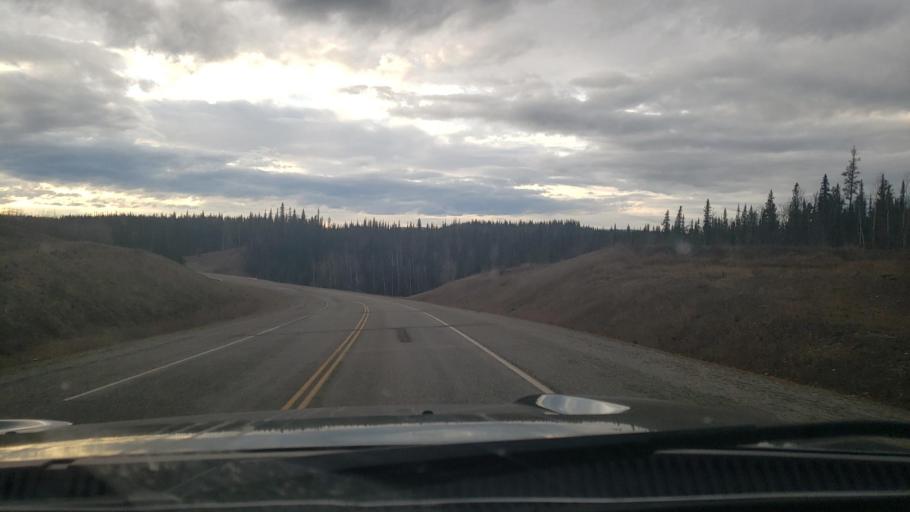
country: CA
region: Yukon
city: Watson Lake
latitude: 59.9978
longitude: -127.6178
